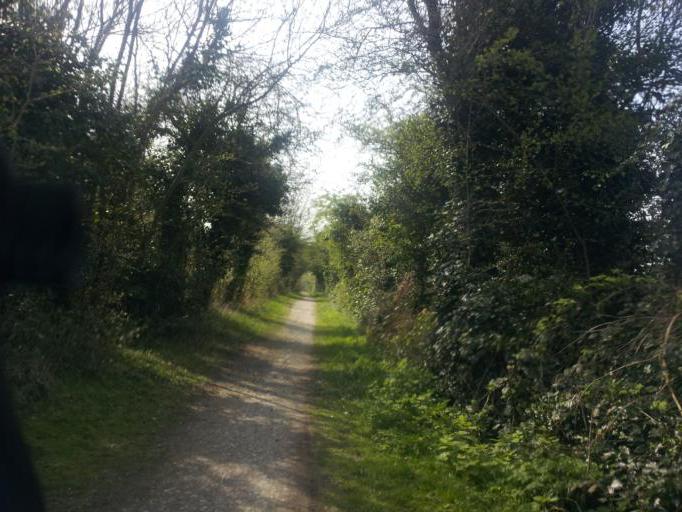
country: GB
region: England
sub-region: Kent
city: Cliffe
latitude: 51.4379
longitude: 0.4428
